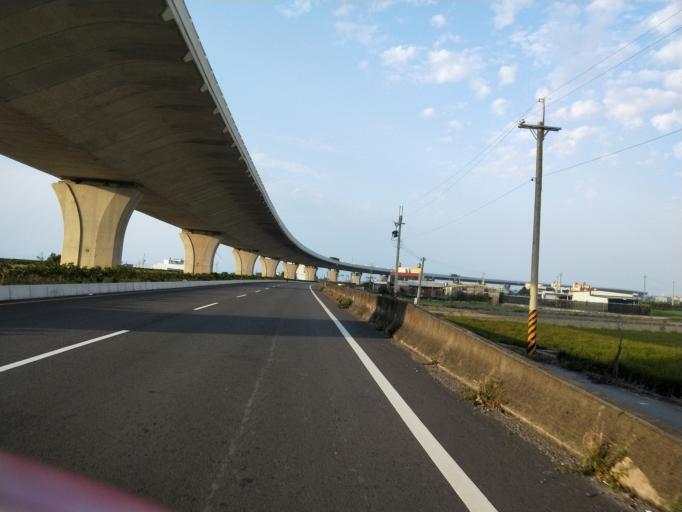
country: TW
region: Taiwan
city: Fengyuan
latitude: 24.4208
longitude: 120.6193
